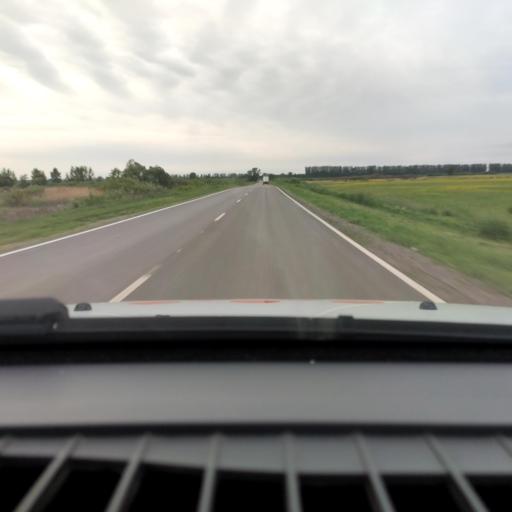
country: RU
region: Voronezj
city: Podkletnoye
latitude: 51.5892
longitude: 39.5149
